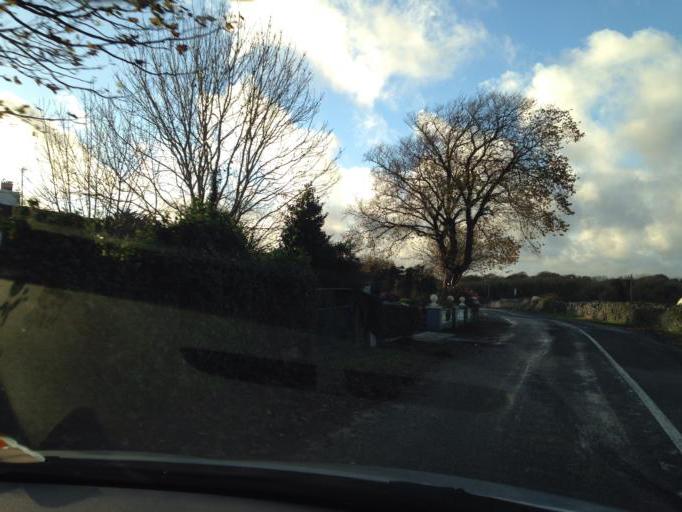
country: IE
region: Connaught
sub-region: County Galway
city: Oranmore
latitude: 53.2723
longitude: -8.9796
